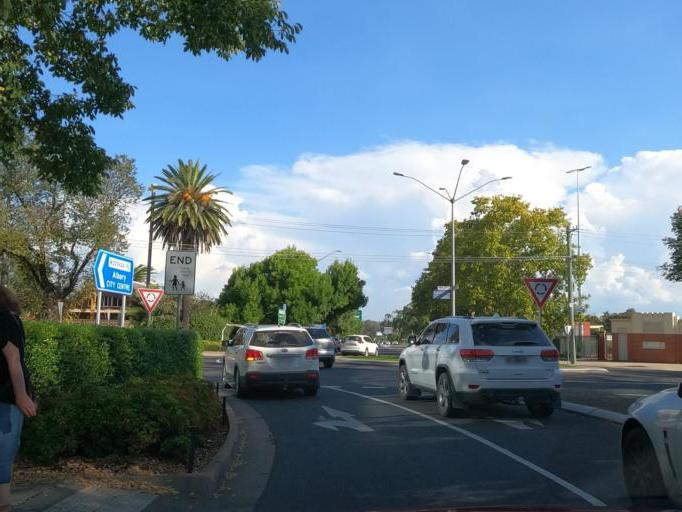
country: AU
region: New South Wales
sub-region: Albury Municipality
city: South Albury
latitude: -36.0819
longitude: 146.9103
